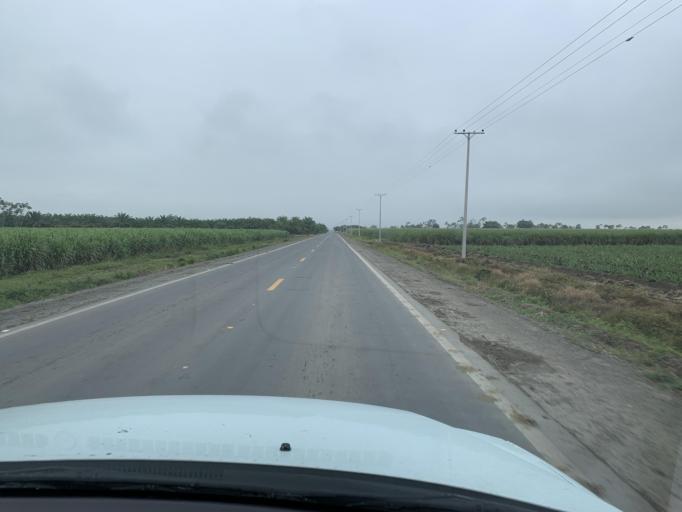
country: EC
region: Guayas
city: Coronel Marcelino Mariduena
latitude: -2.3159
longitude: -79.5148
